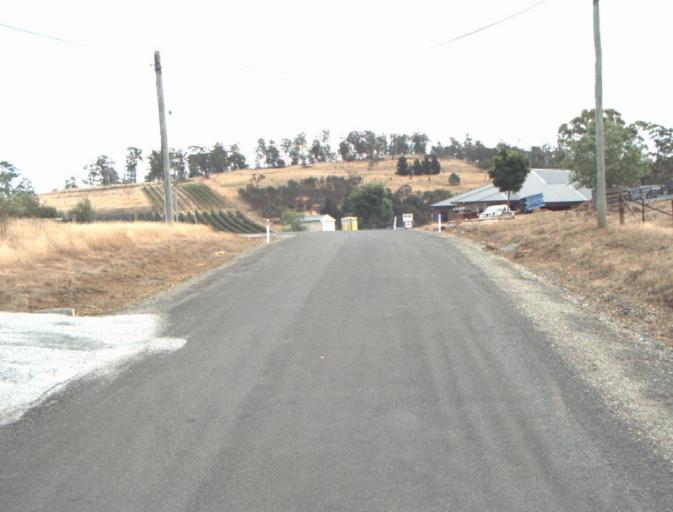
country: AU
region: Tasmania
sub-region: Launceston
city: Mayfield
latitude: -41.3033
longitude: 147.0406
